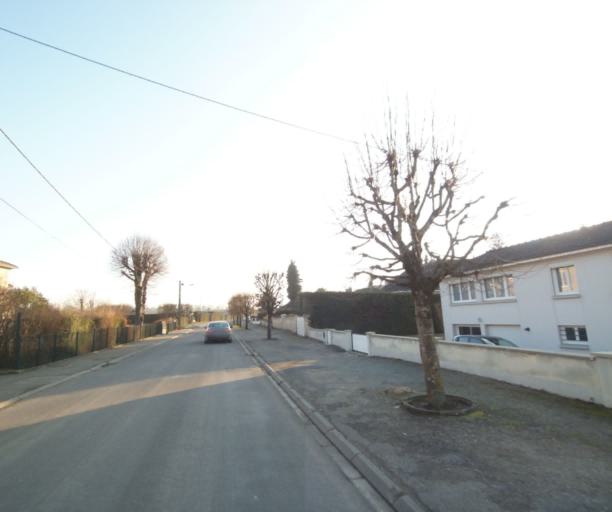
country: FR
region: Champagne-Ardenne
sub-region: Departement de la Haute-Marne
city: Bienville
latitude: 48.5802
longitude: 5.0457
